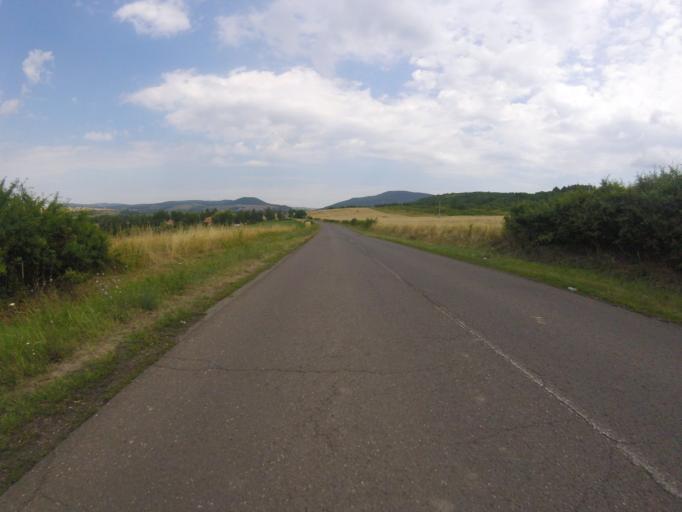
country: HU
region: Nograd
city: Tar
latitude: 47.9424
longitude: 19.7256
